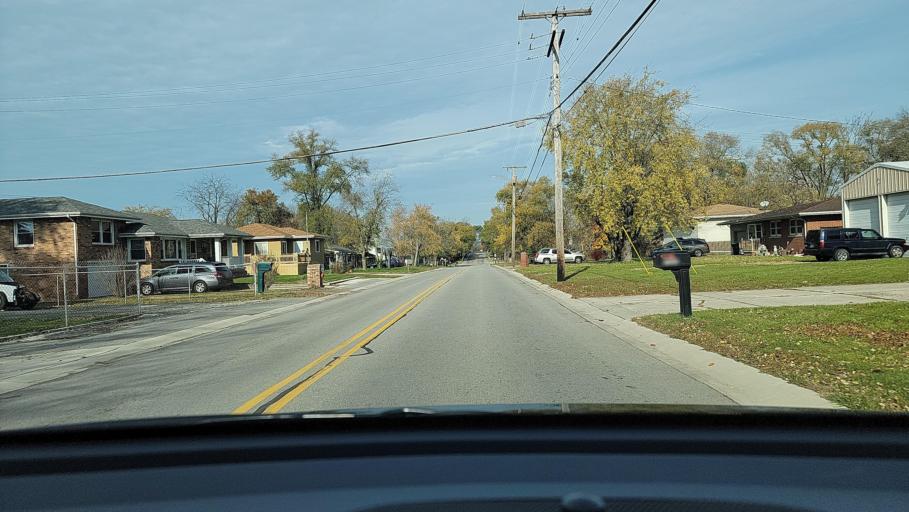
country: US
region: Indiana
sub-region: Lake County
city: Lake Station
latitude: 41.5834
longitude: -87.2123
